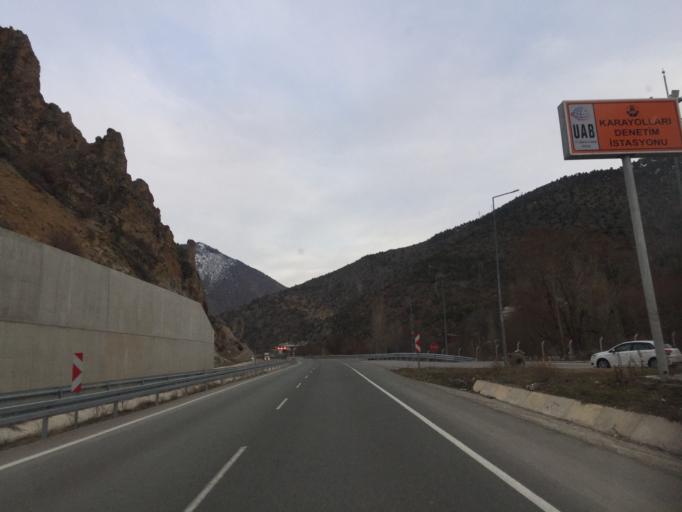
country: TR
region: Gumushane
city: Gumushkhane
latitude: 40.5220
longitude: 39.4022
